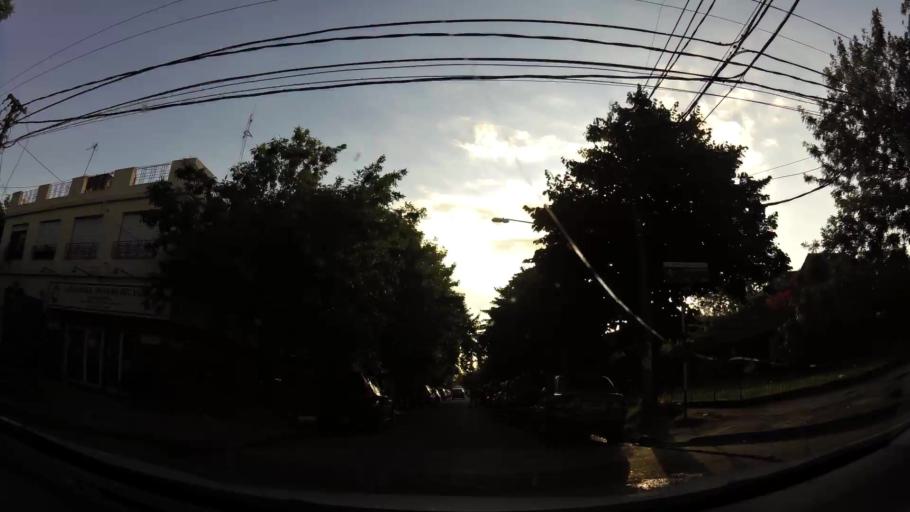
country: AR
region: Buenos Aires
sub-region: Partido de Tigre
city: Tigre
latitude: -34.4579
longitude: -58.6328
